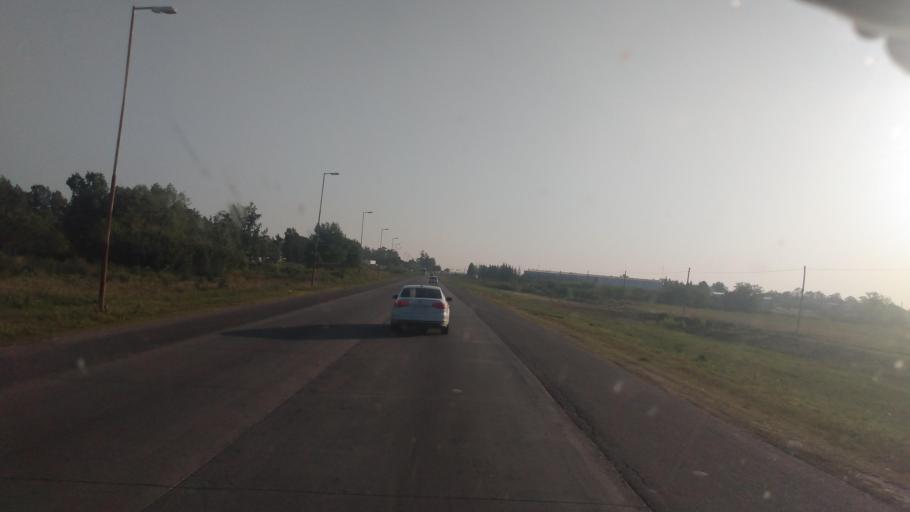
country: AR
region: Buenos Aires
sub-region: Partido de Campana
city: Campana
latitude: -34.1947
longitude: -58.9517
